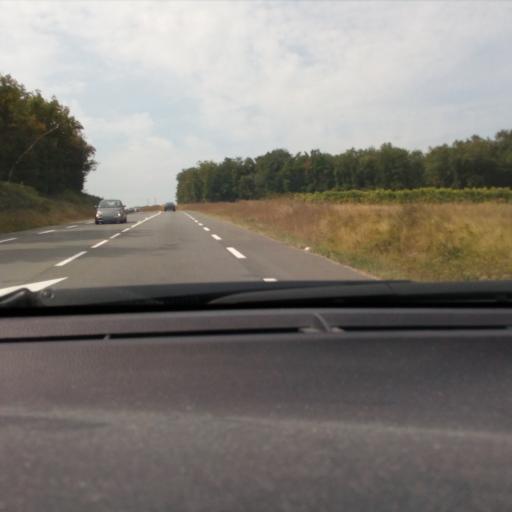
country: FR
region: Poitou-Charentes
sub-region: Departement de la Charente
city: Fleac
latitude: 45.6792
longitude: 0.0797
